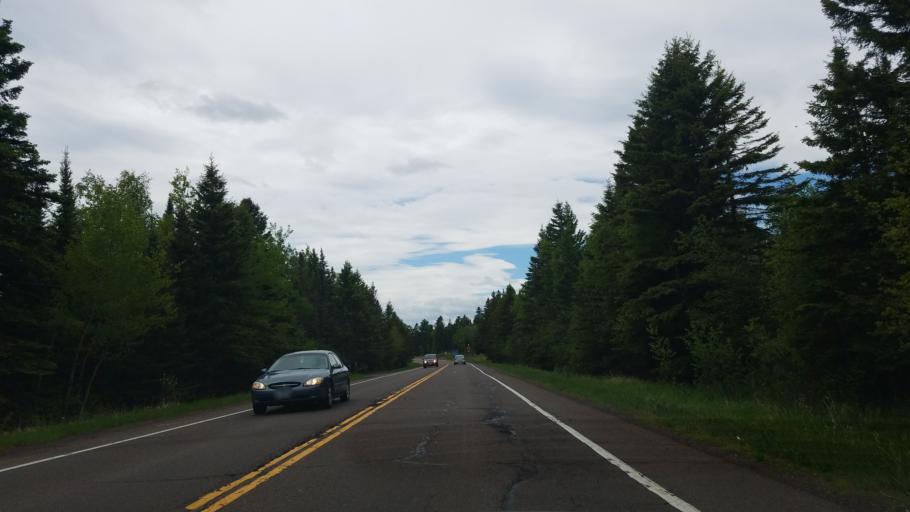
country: US
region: Minnesota
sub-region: Lake County
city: Two Harbors
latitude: 47.0511
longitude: -91.6255
